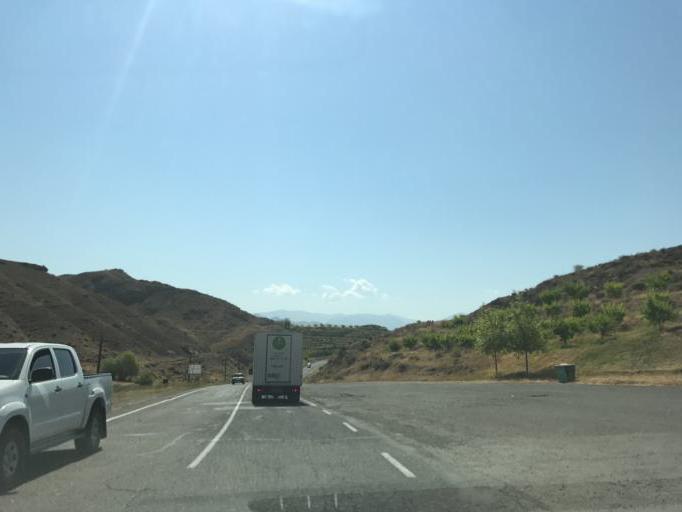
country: AM
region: Vayots' Dzori Marz
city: Yeghegnadzor
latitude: 39.7555
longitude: 45.3521
